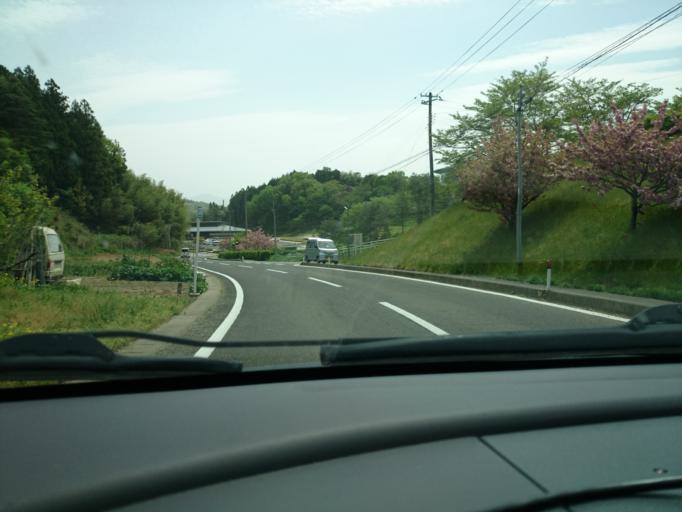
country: JP
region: Fukushima
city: Nihommatsu
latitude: 37.6036
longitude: 140.4305
